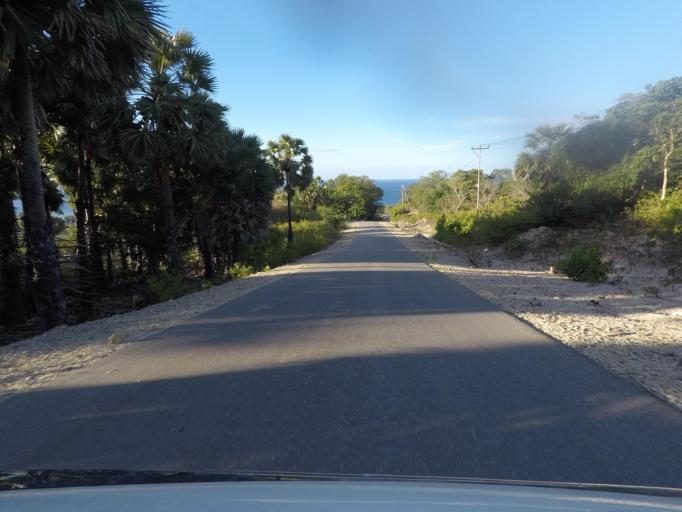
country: TL
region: Lautem
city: Lospalos
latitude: -8.3618
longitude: 127.0536
